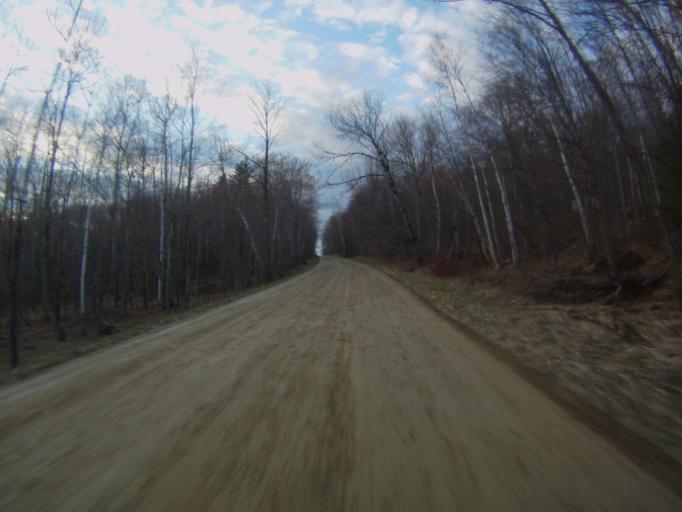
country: US
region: Vermont
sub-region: Rutland County
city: Brandon
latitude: 43.9067
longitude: -73.0170
